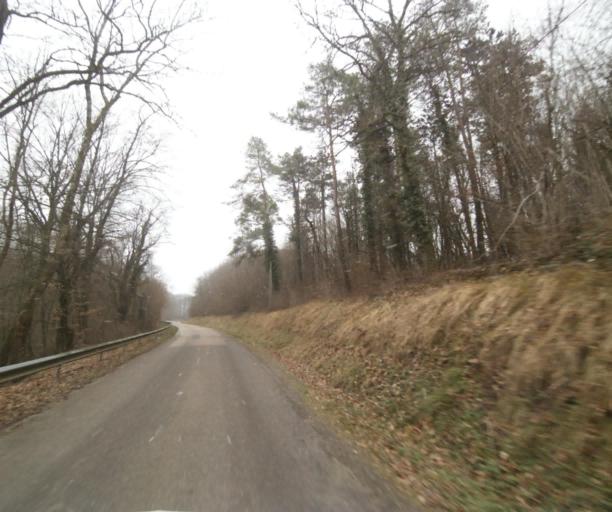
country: FR
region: Champagne-Ardenne
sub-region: Departement de la Haute-Marne
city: Chevillon
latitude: 48.5200
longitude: 5.0915
